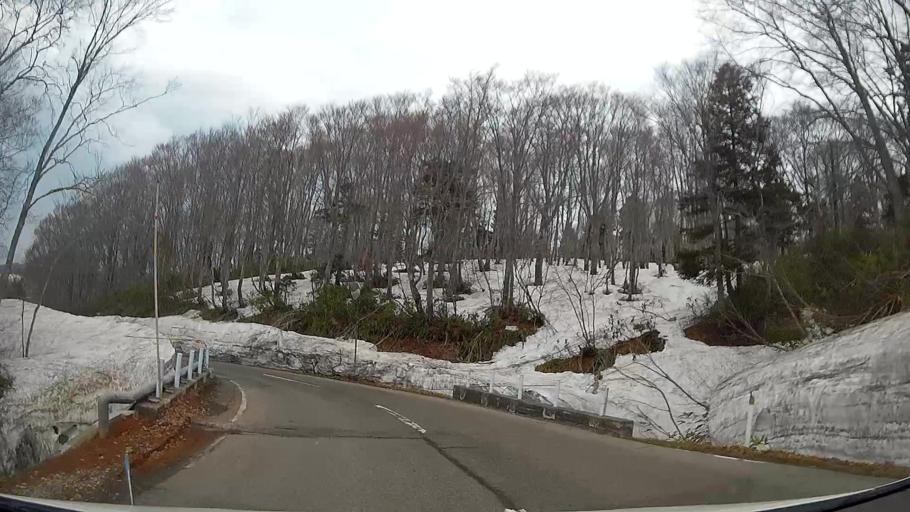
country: JP
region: Aomori
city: Aomori Shi
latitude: 40.6450
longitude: 140.8590
